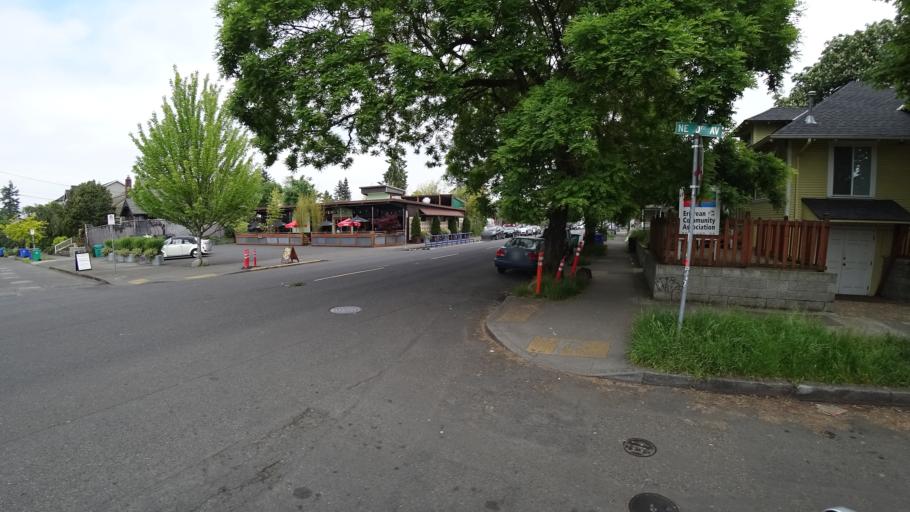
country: US
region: Oregon
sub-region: Multnomah County
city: Portland
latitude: 45.5590
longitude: -122.6556
